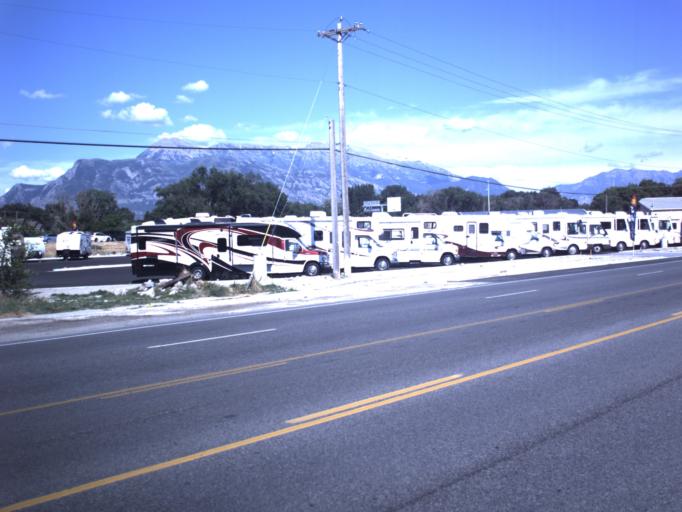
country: US
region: Utah
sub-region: Utah County
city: Lehi
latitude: 40.4109
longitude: -111.8665
